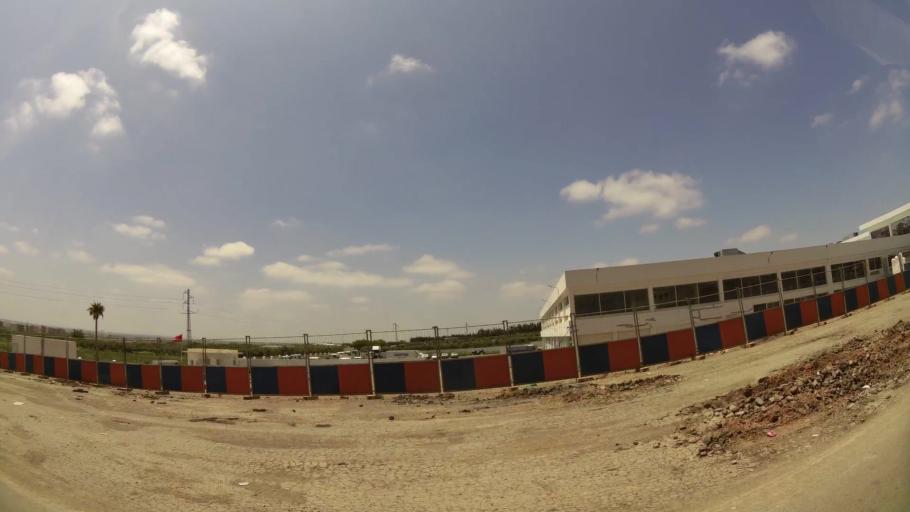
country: MA
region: Fes-Boulemane
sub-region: Fes
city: Fes
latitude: 34.0418
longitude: -5.0627
